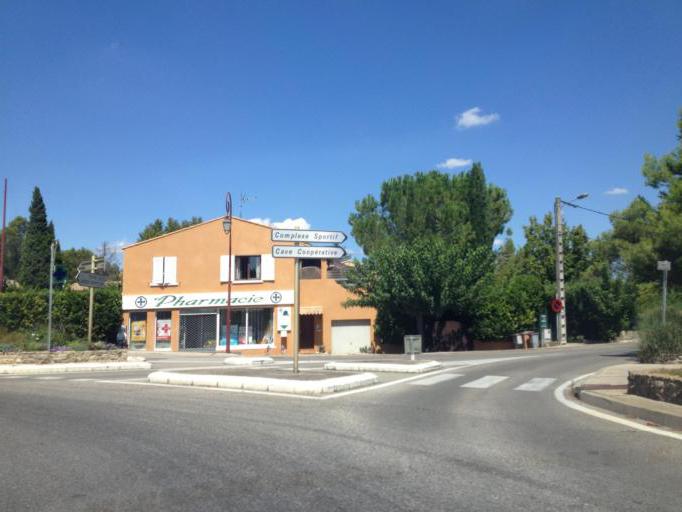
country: FR
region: Languedoc-Roussillon
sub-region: Departement du Gard
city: Sauveterre
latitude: 44.0241
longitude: 4.7946
